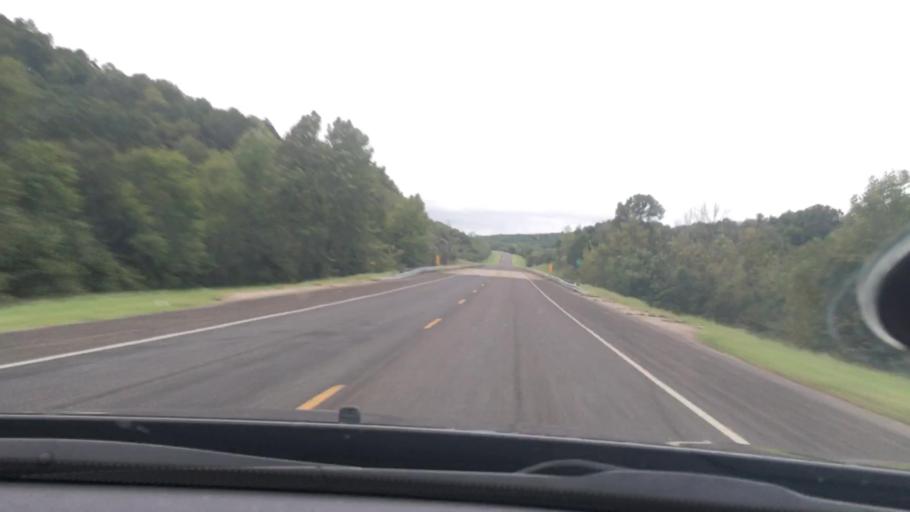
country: US
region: Oklahoma
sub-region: Sequoyah County
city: Vian
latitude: 35.5385
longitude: -94.9697
